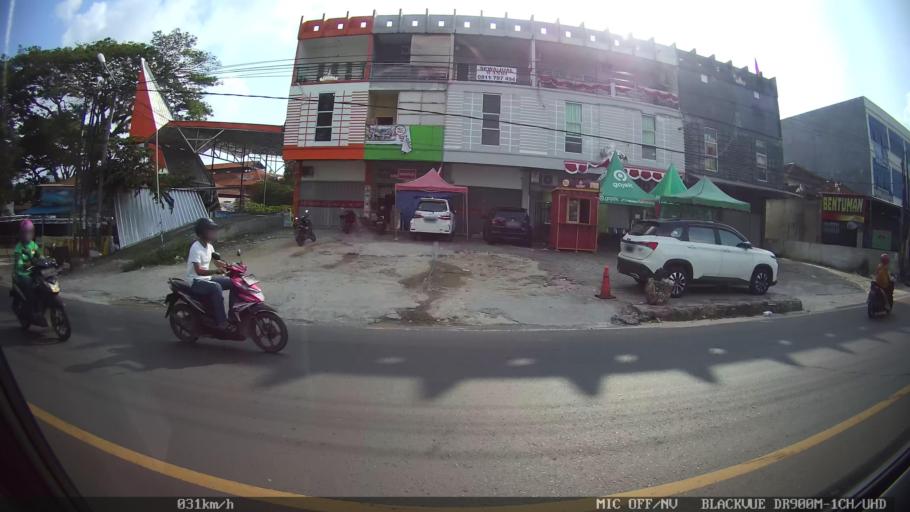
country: ID
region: Lampung
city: Bandarlampung
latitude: -5.4372
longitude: 105.2560
